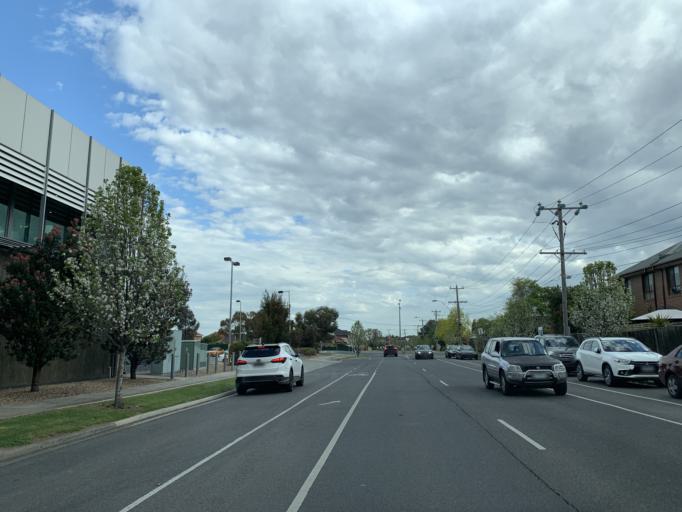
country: AU
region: Victoria
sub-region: Moonee Valley
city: Keilor East
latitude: -37.7497
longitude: 144.8602
